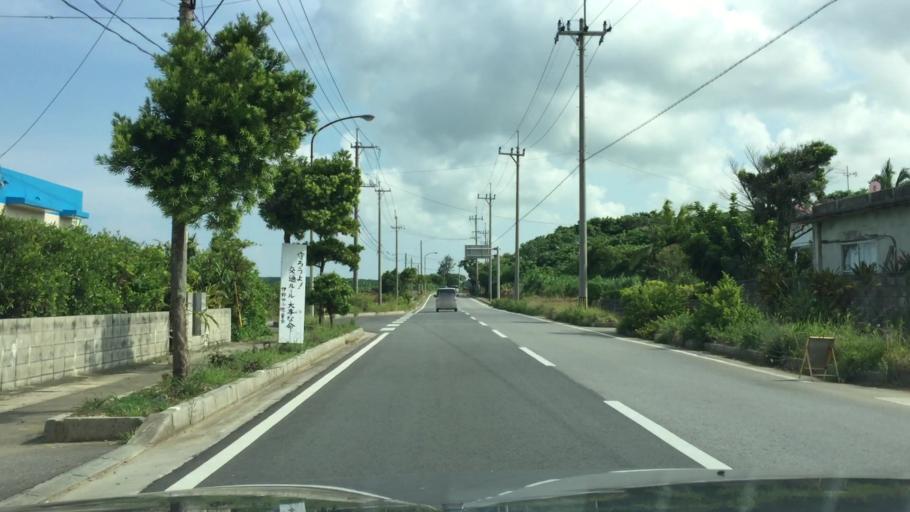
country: JP
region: Okinawa
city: Ishigaki
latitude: 24.4624
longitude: 124.2503
